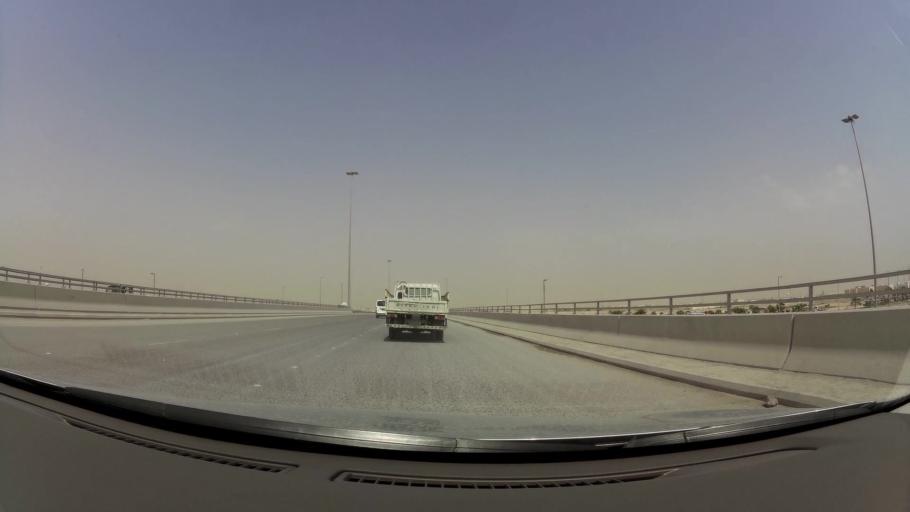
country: QA
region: Baladiyat ar Rayyan
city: Ar Rayyan
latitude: 25.2107
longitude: 51.4068
